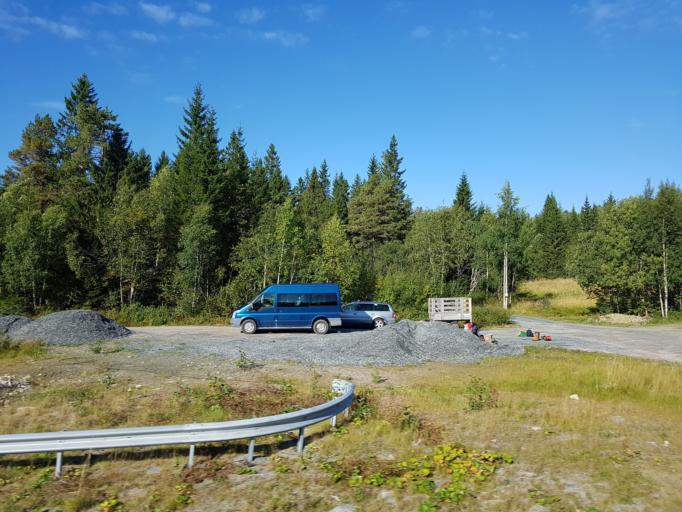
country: NO
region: Sor-Trondelag
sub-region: Trondheim
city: Trondheim
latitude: 63.6087
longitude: 10.2375
